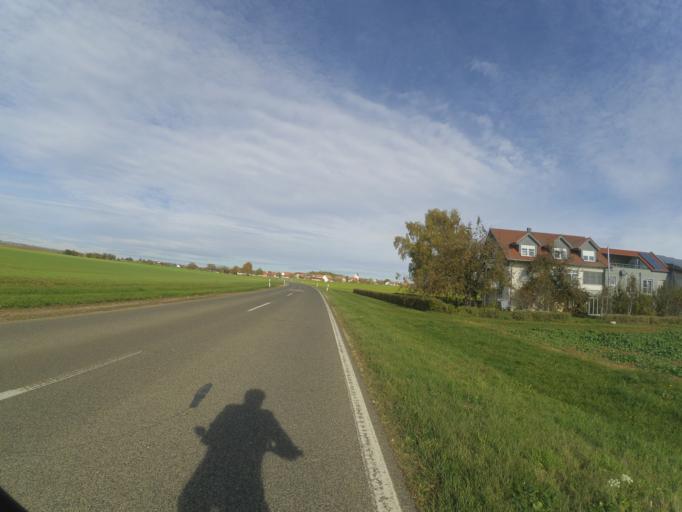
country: DE
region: Baden-Wuerttemberg
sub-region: Tuebingen Region
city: Lonsee
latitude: 48.5765
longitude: 9.9181
